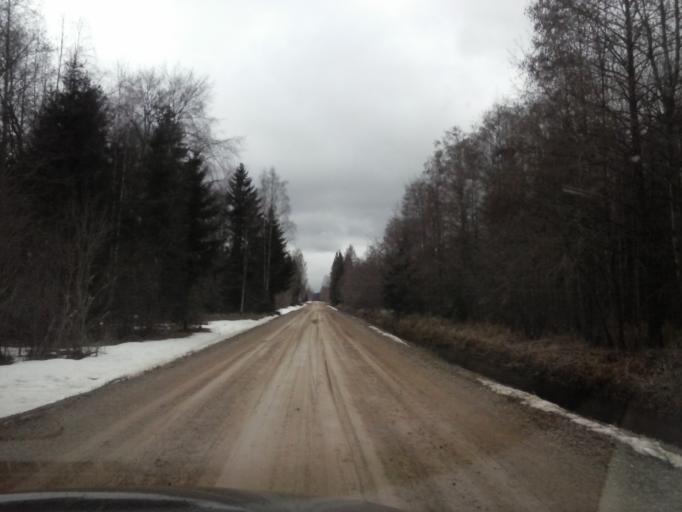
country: EE
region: Jogevamaa
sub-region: Mustvee linn
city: Mustvee
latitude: 59.0837
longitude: 26.8687
